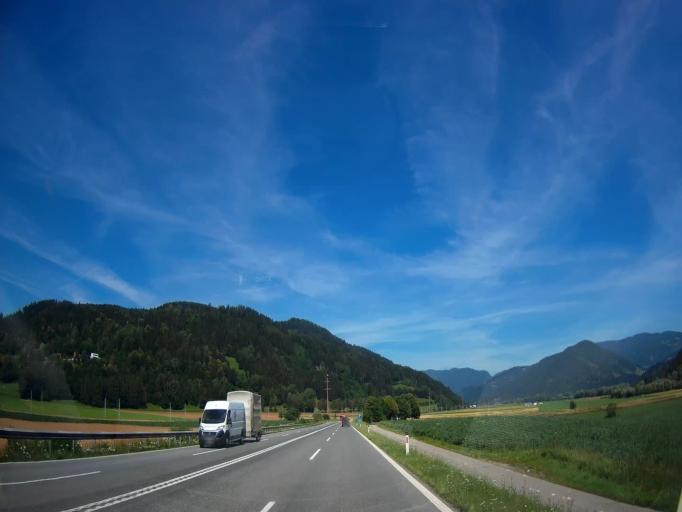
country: AT
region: Carinthia
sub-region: Politischer Bezirk Sankt Veit an der Glan
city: Micheldorf
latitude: 46.9182
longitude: 14.4332
